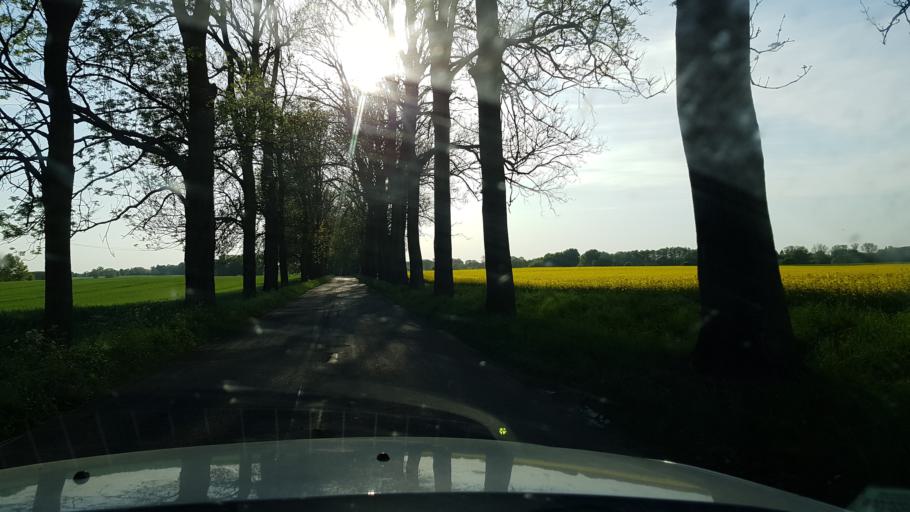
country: PL
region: West Pomeranian Voivodeship
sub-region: Powiat lobeski
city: Dobra
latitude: 53.5759
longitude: 15.2597
